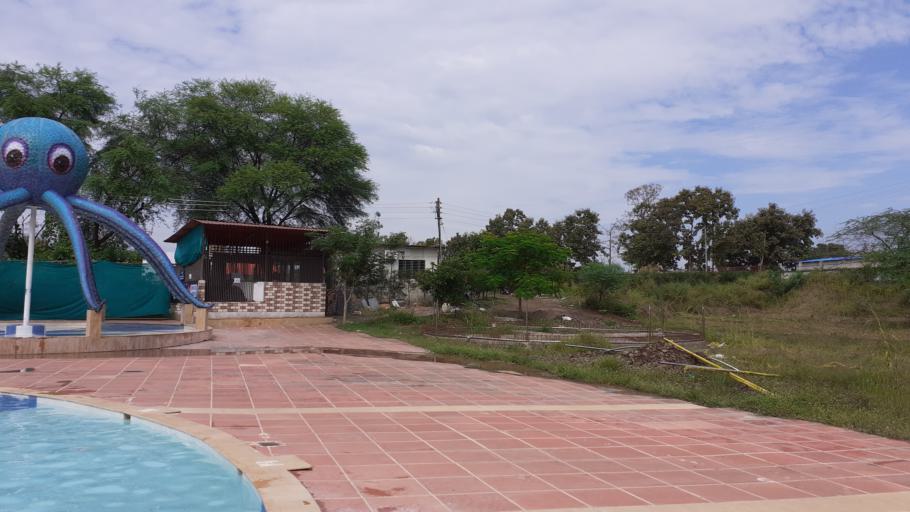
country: IN
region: Madhya Pradesh
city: Khapa
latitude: 21.3352
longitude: 79.0034
